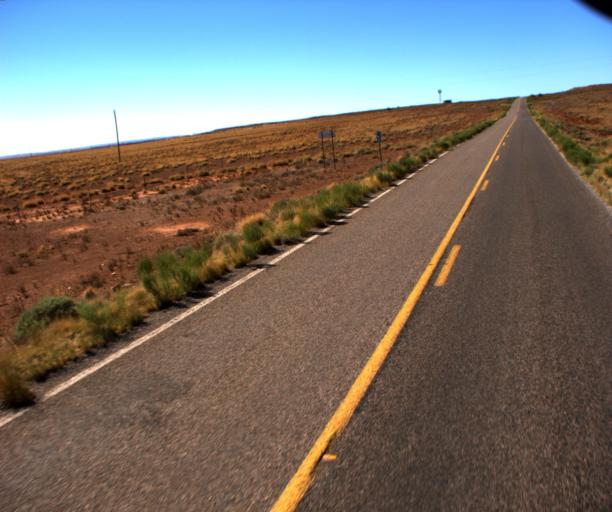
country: US
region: Arizona
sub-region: Coconino County
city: LeChee
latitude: 35.2471
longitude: -110.9610
